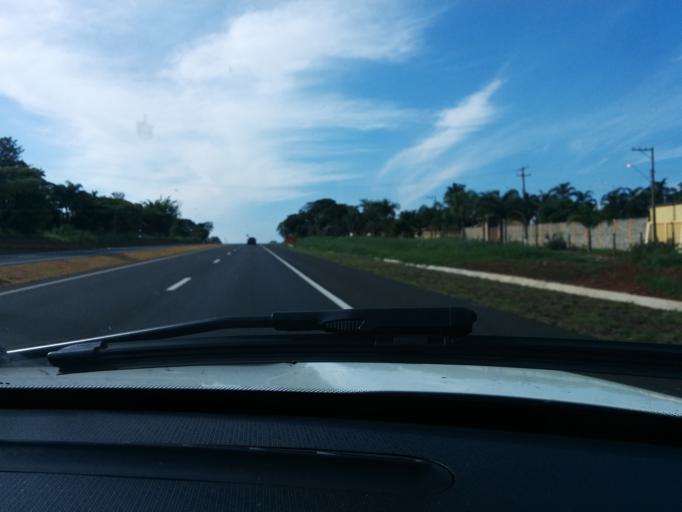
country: BR
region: Sao Paulo
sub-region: Franca
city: Franca
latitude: -20.4542
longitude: -47.4175
